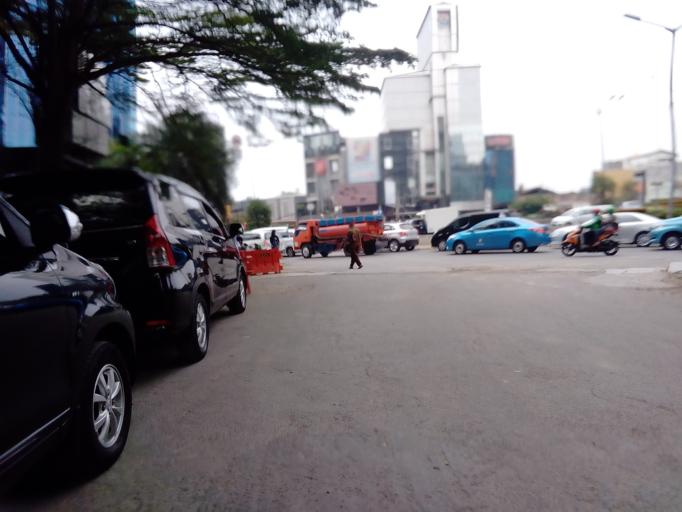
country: ID
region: Jakarta Raya
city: Jakarta
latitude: -6.1996
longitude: 106.8225
